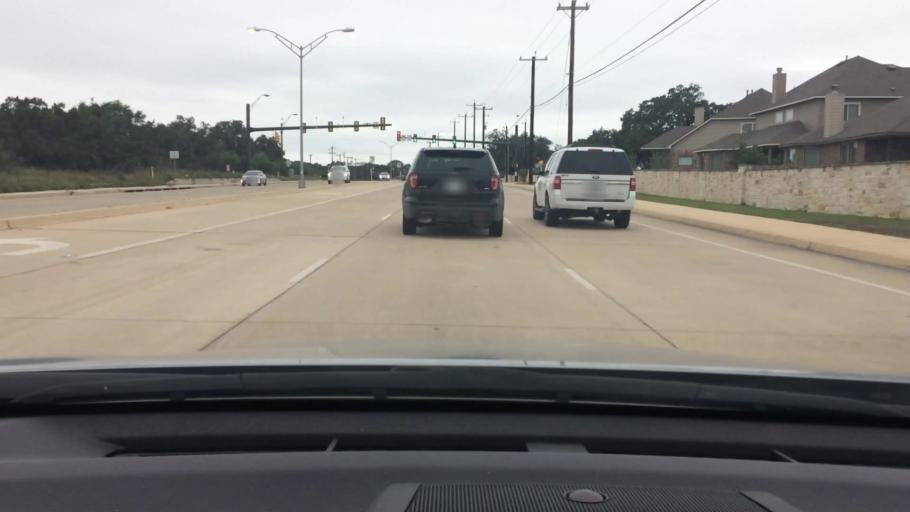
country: US
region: Texas
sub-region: Bexar County
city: Hollywood Park
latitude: 29.6372
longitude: -98.4241
